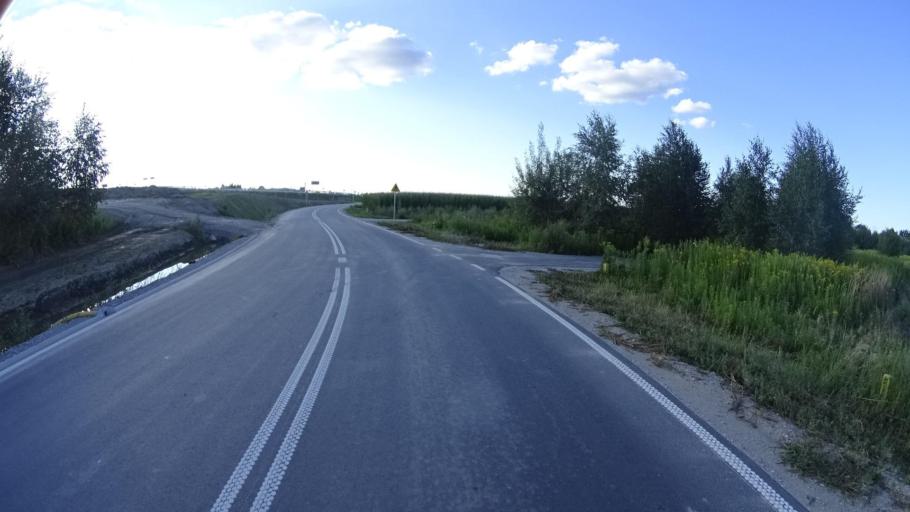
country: PL
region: Masovian Voivodeship
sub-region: Powiat piaseczynski
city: Mysiadlo
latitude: 52.1153
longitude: 20.9901
